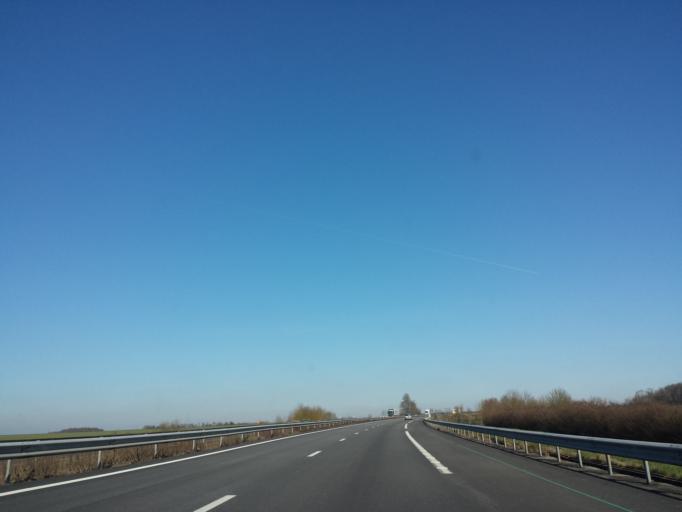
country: FR
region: Picardie
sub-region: Departement de l'Oise
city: Saint-Crepin-Ibouvillers
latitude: 49.2885
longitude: 2.0727
